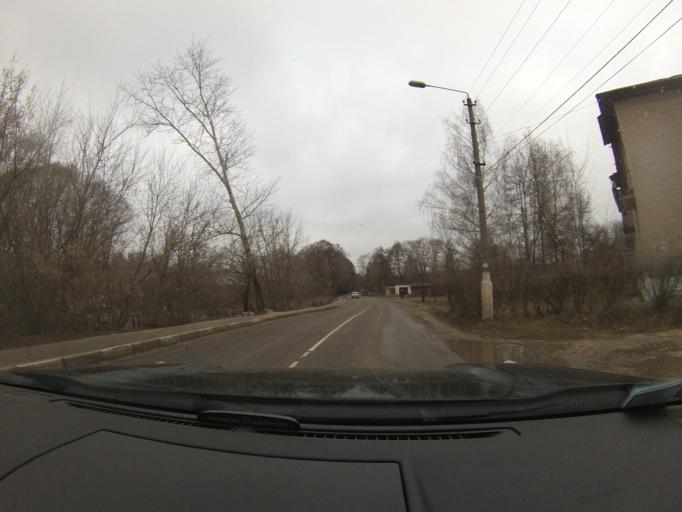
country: RU
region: Moskovskaya
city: Peski
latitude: 55.2617
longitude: 38.7625
